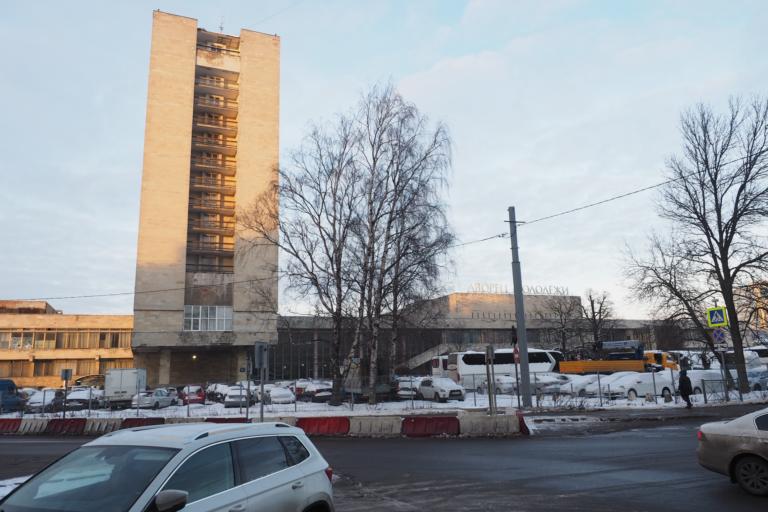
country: RU
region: St.-Petersburg
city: Novaya Derevnya
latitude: 59.9703
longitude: 30.2879
